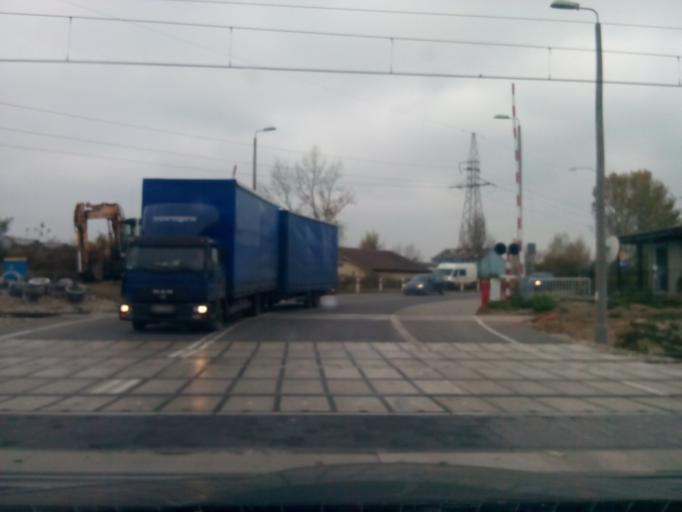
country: PL
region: Masovian Voivodeship
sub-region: Powiat pruszkowski
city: Otrebusy
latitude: 52.1571
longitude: 20.7652
